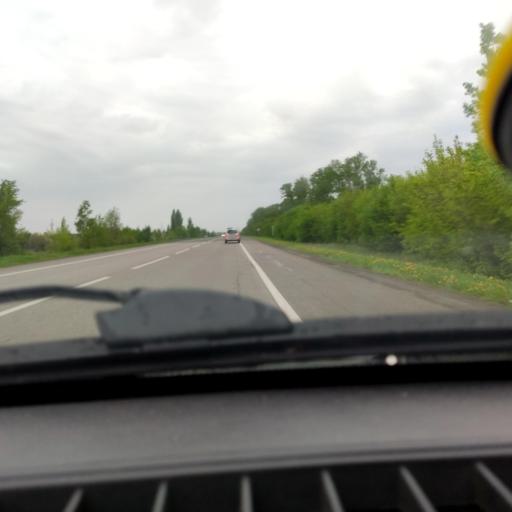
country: RU
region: Samara
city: Tol'yatti
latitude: 53.7000
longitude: 49.4206
